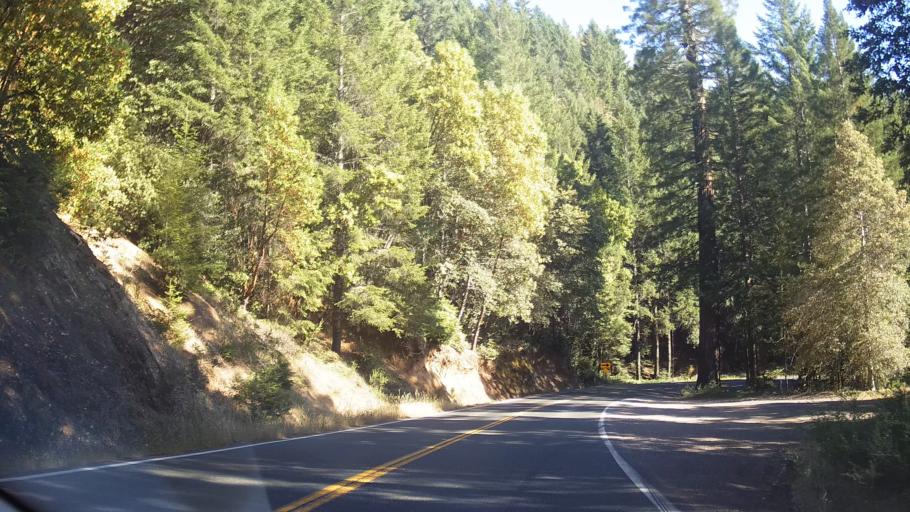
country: US
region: California
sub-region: Mendocino County
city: Brooktrails
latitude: 39.3918
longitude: -123.4662
